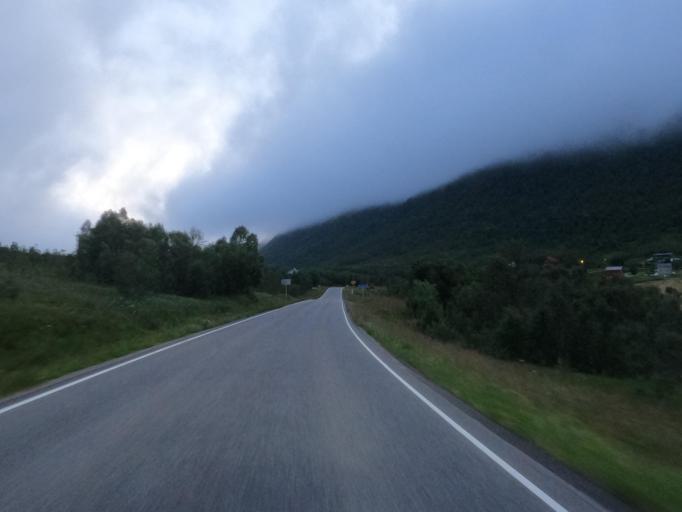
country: NO
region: Nordland
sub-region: Lodingen
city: Lodingen
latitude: 68.6141
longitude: 15.7675
